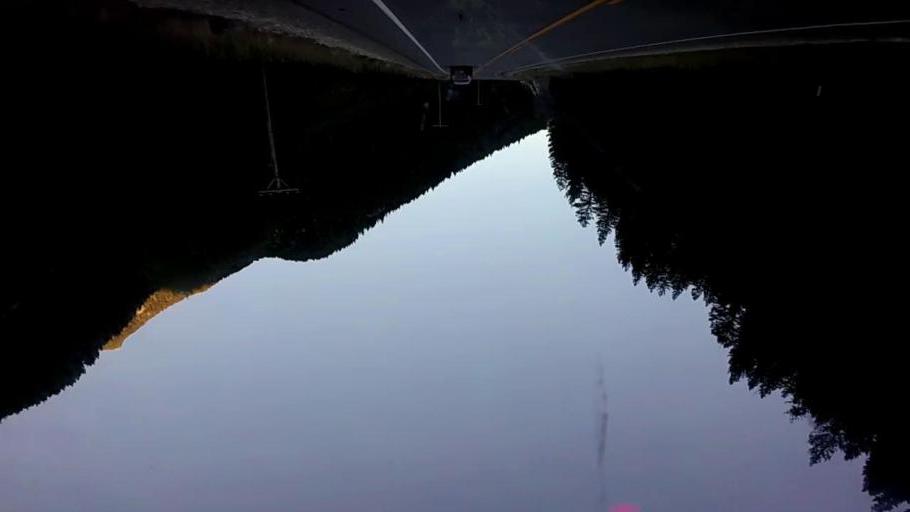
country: US
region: Utah
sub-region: Salt Lake County
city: Mount Olympus
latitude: 40.6423
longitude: -111.6790
